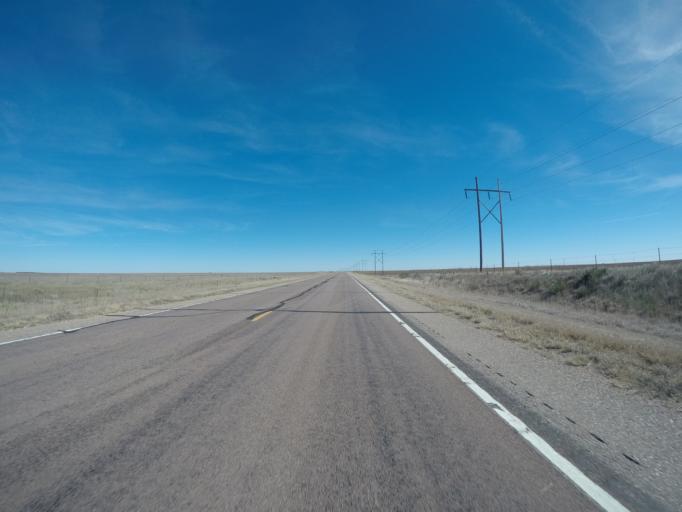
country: US
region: Colorado
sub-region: Yuma County
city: Yuma
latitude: 39.6549
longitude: -102.8096
